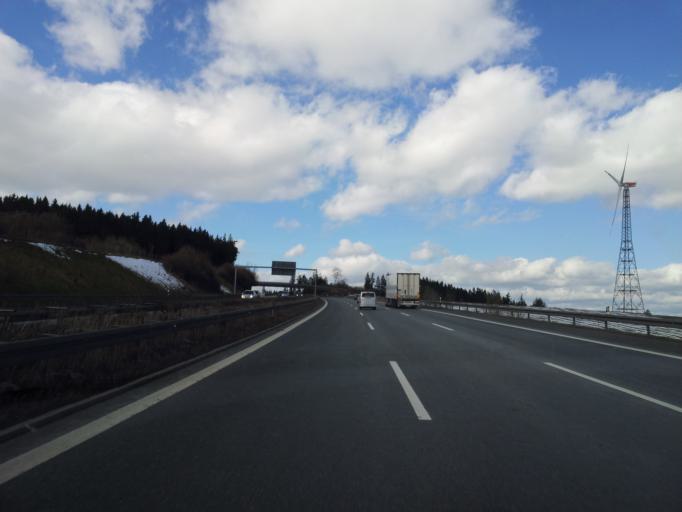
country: DE
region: Bavaria
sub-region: Upper Franconia
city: Munchberg
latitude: 50.2172
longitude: 11.7822
